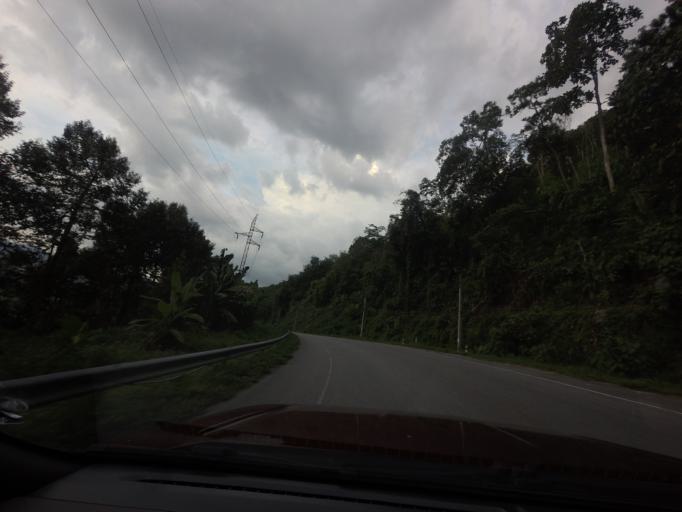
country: TH
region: Yala
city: Than To
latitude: 5.9911
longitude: 101.1923
